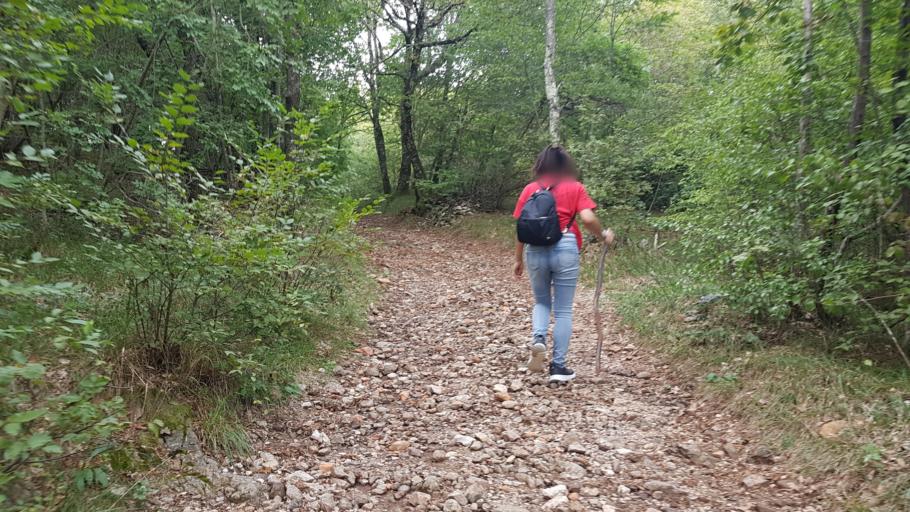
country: IT
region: Friuli Venezia Giulia
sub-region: Provincia di Trieste
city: Zolla
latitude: 45.7361
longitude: 13.7925
